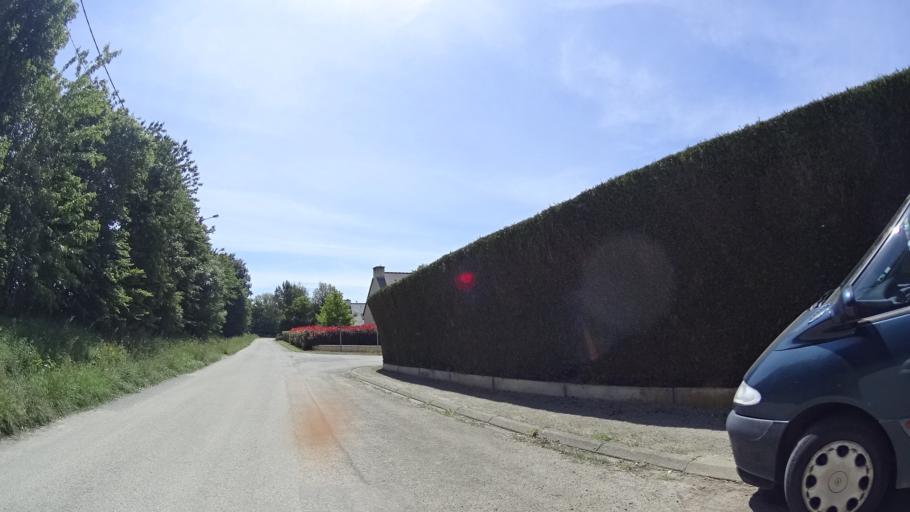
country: FR
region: Brittany
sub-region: Departement d'Ille-et-Vilaine
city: Iffendic
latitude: 48.1189
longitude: -2.0322
